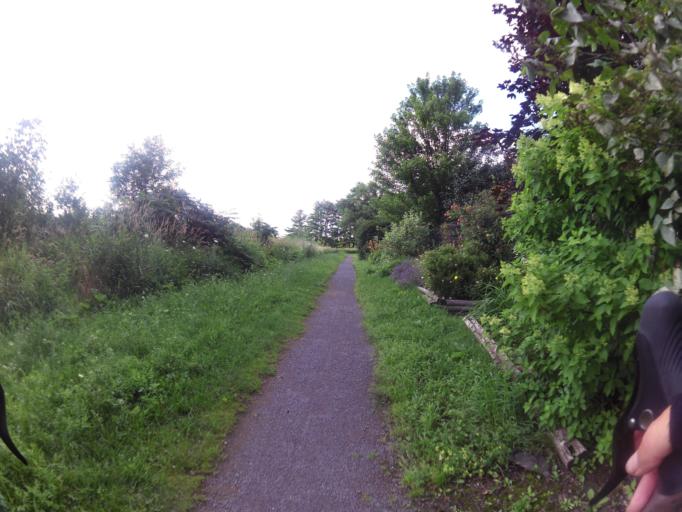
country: CA
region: Ontario
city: Ottawa
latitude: 45.2832
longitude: -75.6922
